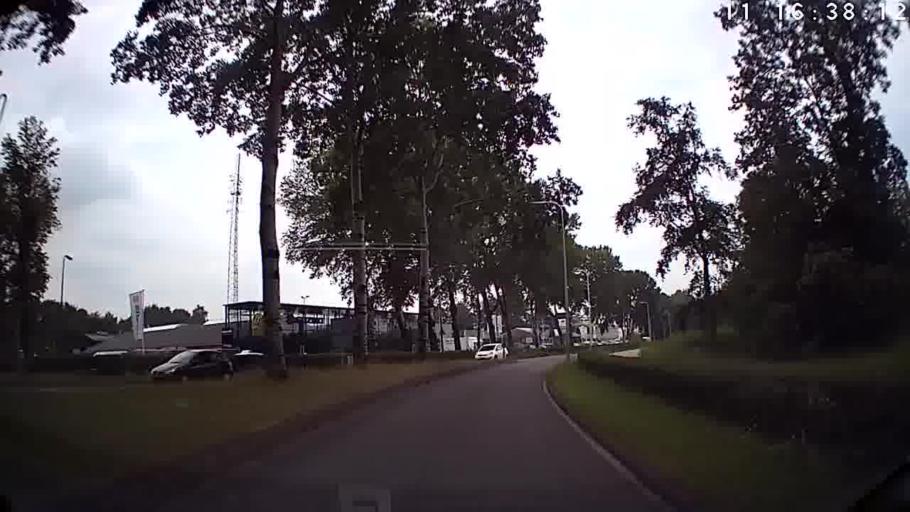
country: NL
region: Overijssel
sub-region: Gemeente Zwolle
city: Zwolle
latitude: 52.5039
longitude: 6.1191
